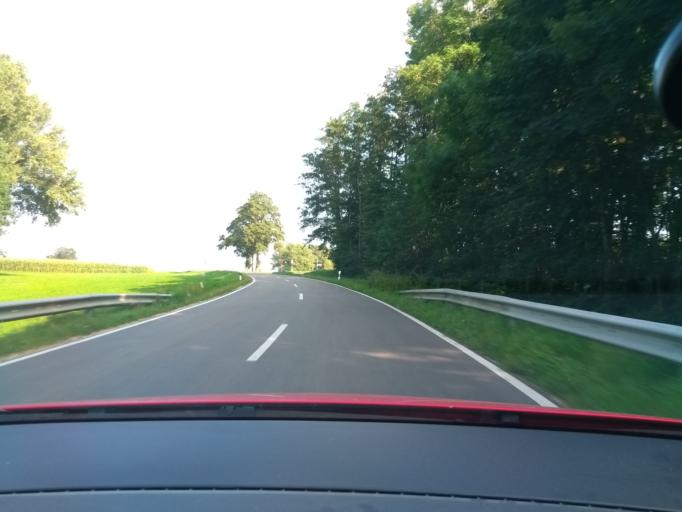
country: DE
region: Bavaria
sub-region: Upper Bavaria
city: Altomunster
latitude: 48.3992
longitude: 11.3053
